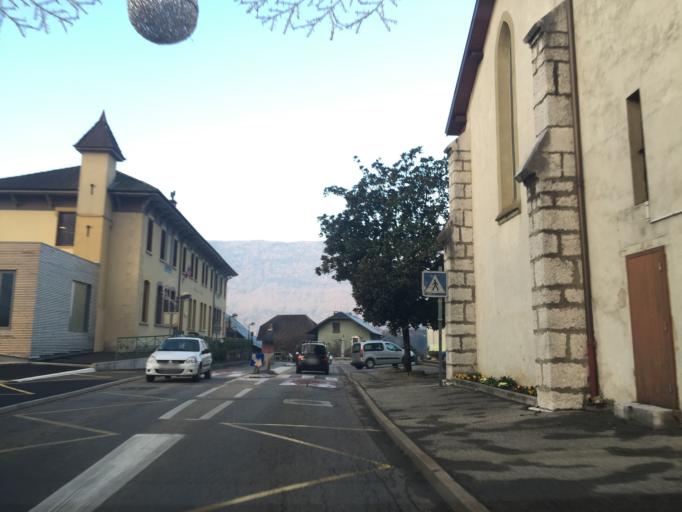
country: FR
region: Rhone-Alpes
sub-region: Departement de la Savoie
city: Viviers-du-Lac
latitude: 45.6484
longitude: 5.9064
